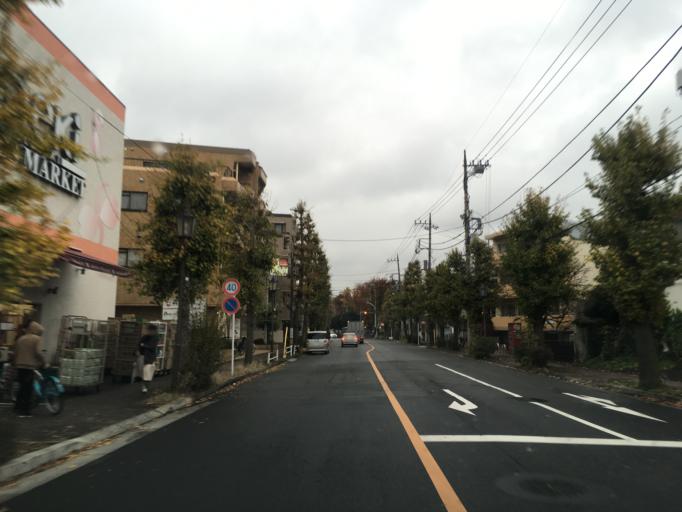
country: JP
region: Tokyo
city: Kokubunji
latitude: 35.6866
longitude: 139.4406
